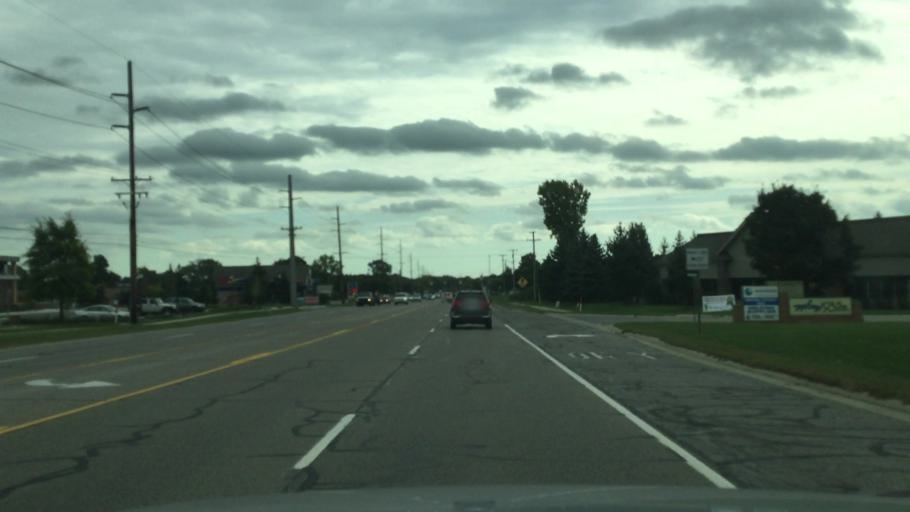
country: US
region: Michigan
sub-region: Livingston County
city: Howell
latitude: 42.5838
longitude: -83.8660
